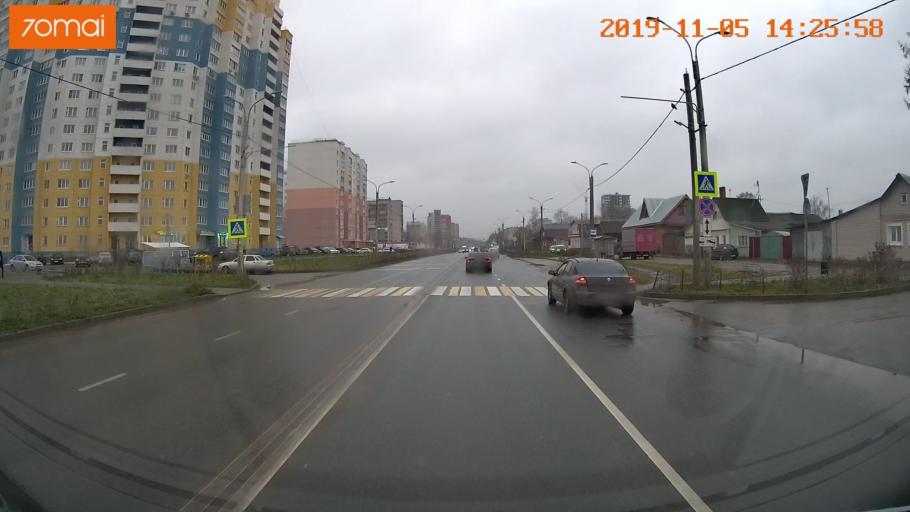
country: RU
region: Ivanovo
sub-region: Gorod Ivanovo
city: Ivanovo
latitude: 56.9712
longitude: 40.9896
